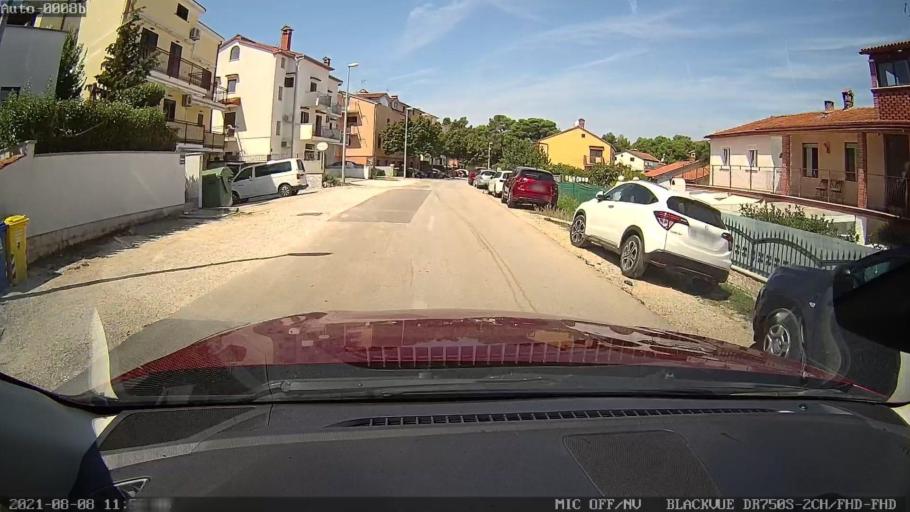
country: HR
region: Istarska
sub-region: Grad Rovinj
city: Rovinj
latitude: 45.0841
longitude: 13.6470
